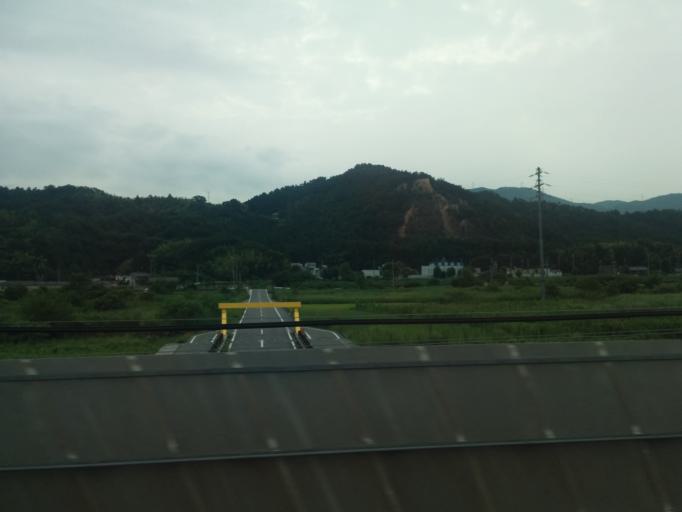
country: JP
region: Shiga Prefecture
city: Hikone
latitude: 35.2936
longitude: 136.2823
